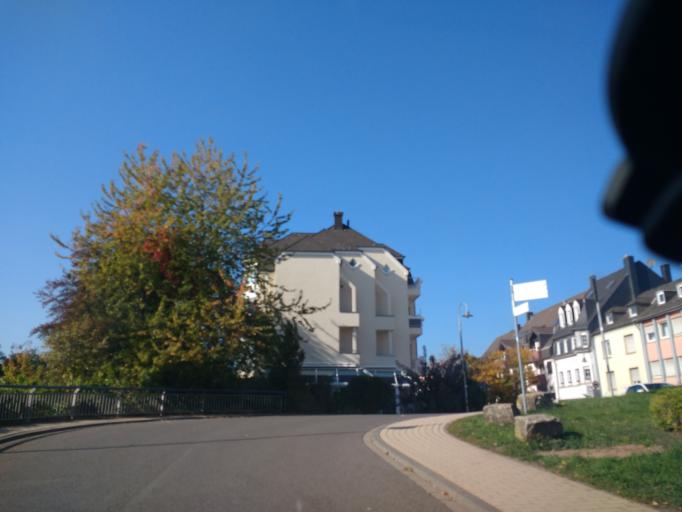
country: DE
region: Rheinland-Pfalz
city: Konz
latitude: 49.6972
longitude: 6.5752
